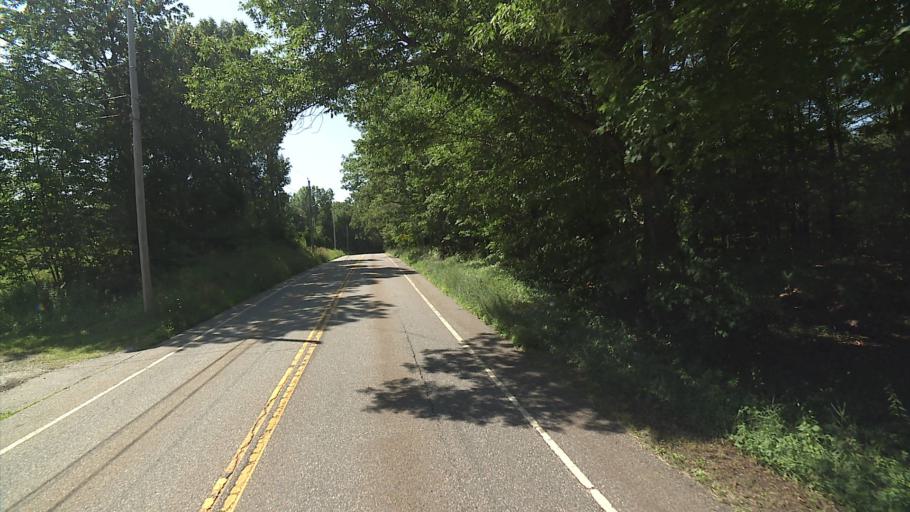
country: US
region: Connecticut
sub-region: Litchfield County
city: New Preston
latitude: 41.7742
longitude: -73.3531
